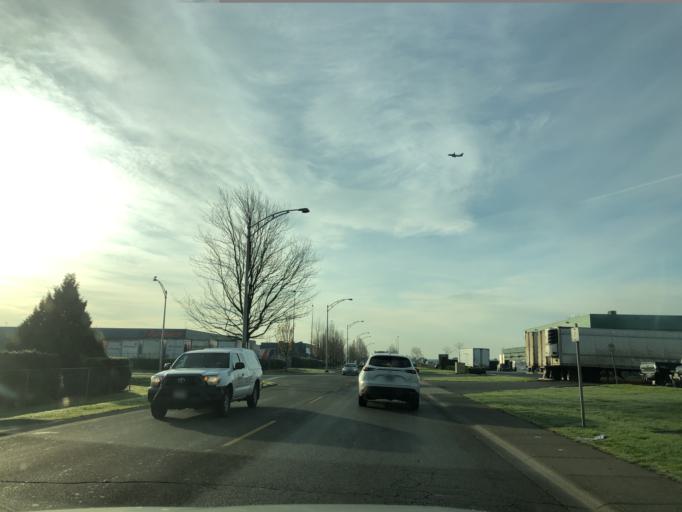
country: CA
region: British Columbia
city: Richmond
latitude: 49.1909
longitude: -123.1588
